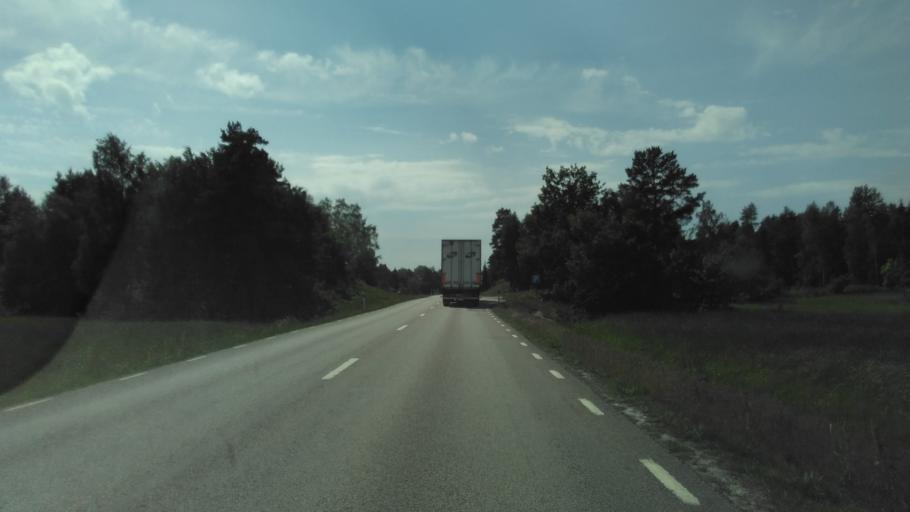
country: SE
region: Vaestra Goetaland
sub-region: Vara Kommun
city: Vara
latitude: 58.4216
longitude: 12.8729
